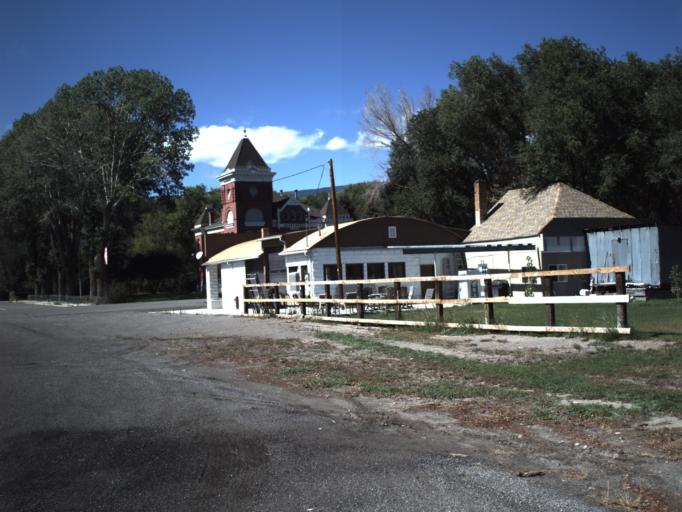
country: US
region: Utah
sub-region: Piute County
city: Junction
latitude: 38.2369
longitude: -112.2191
